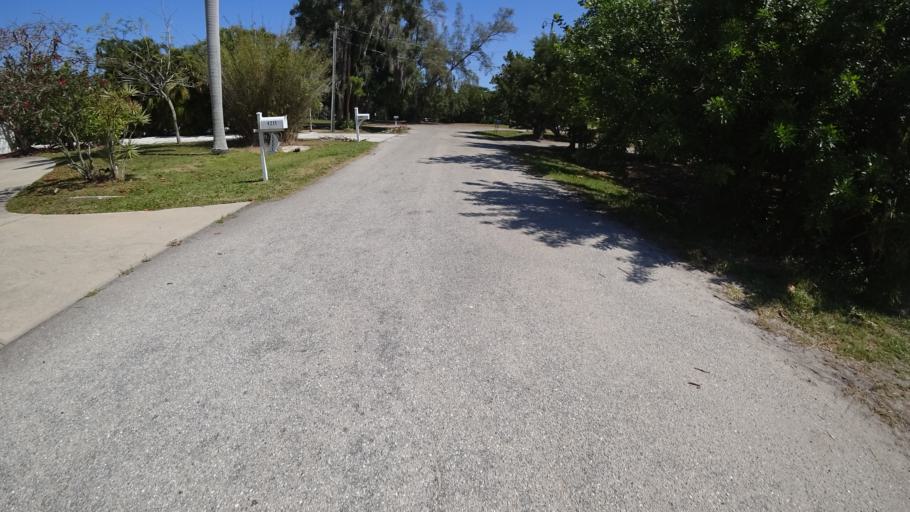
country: US
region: Florida
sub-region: Manatee County
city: Cortez
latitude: 27.4724
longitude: -82.6899
